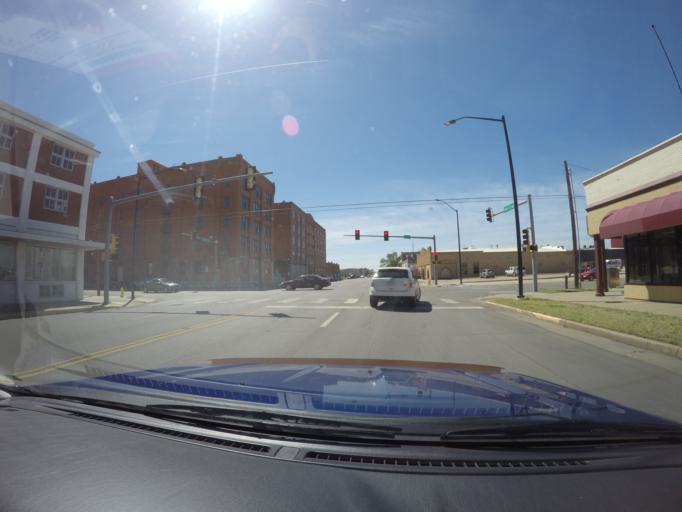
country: US
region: Kansas
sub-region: Saline County
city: Salina
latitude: 38.8454
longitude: -97.6091
